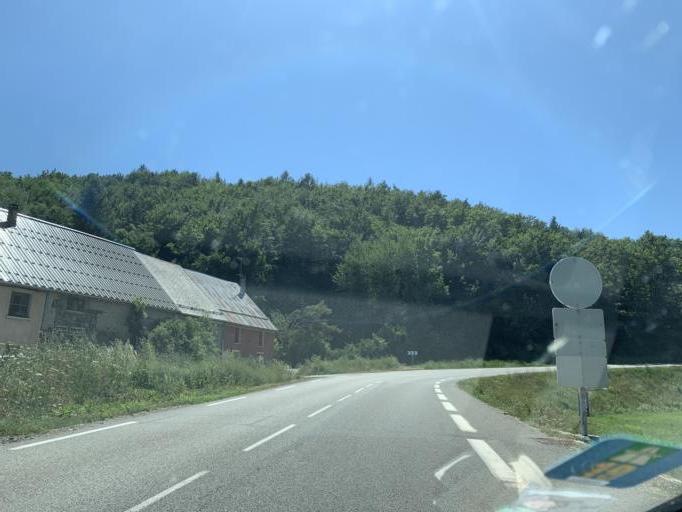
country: FR
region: Provence-Alpes-Cote d'Azur
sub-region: Departement des Hautes-Alpes
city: Saint-Bonnet-en-Champsaur
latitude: 44.6383
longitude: 6.1426
